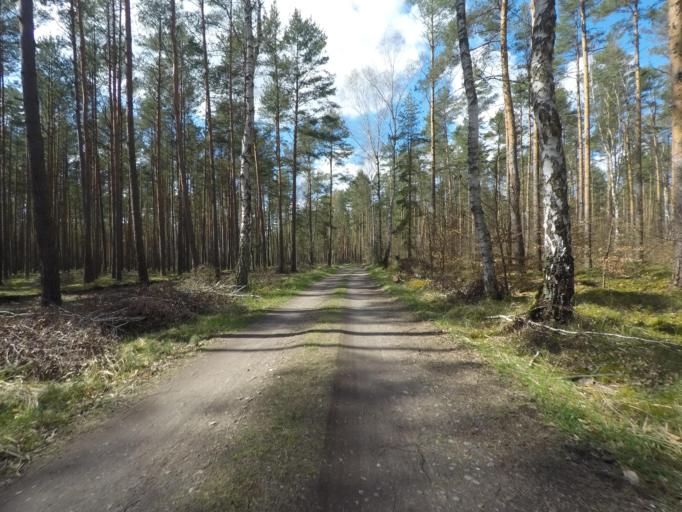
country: DE
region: Brandenburg
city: Melchow
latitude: 52.8202
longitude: 13.6871
